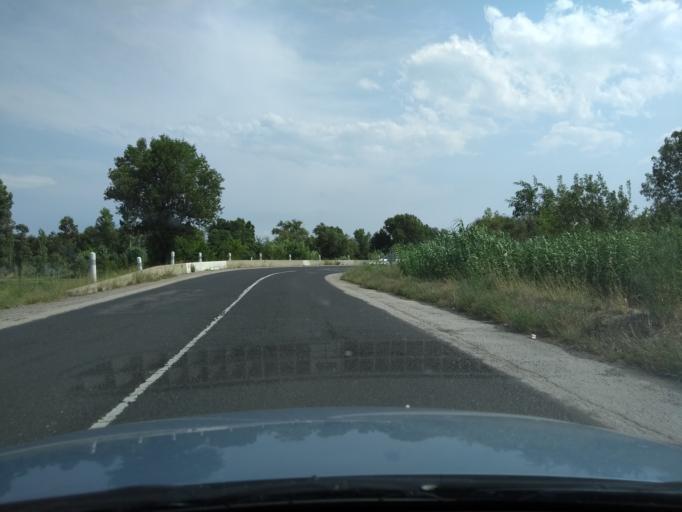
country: FR
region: Languedoc-Roussillon
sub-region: Departement des Pyrenees-Orientales
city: Pezilla-la-Riviere
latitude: 42.6865
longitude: 2.7530
